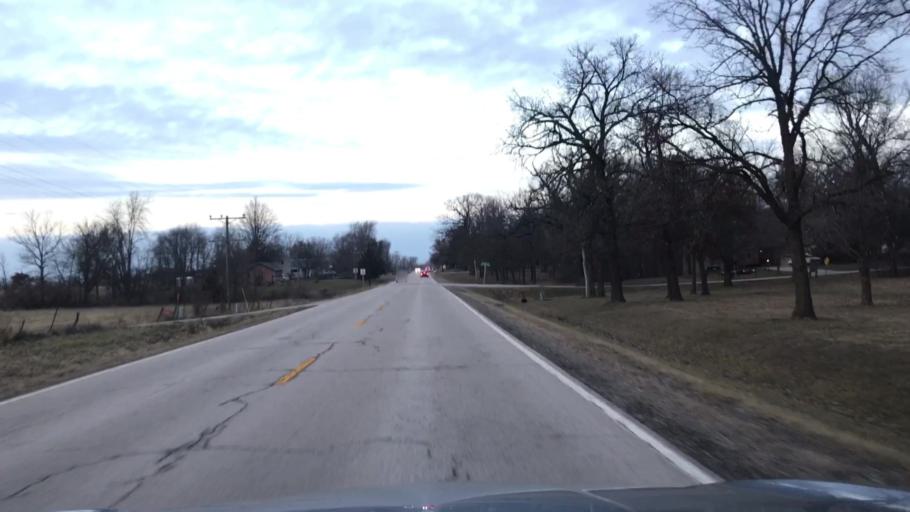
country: US
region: Illinois
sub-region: McLean County
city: Hudson
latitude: 40.6519
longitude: -88.9368
